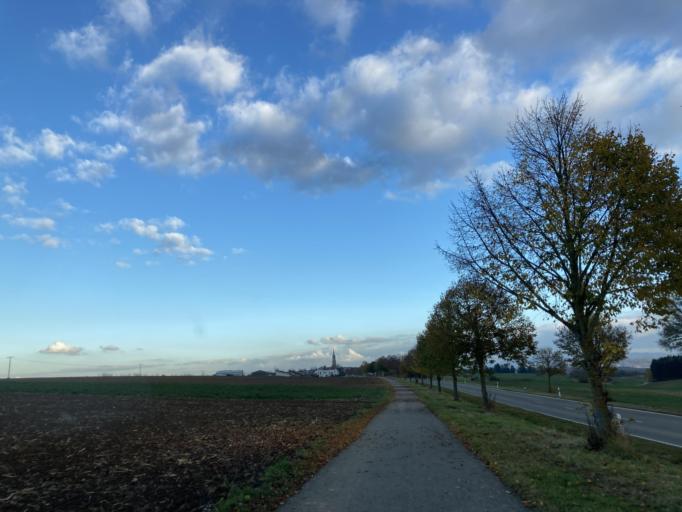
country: DE
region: Baden-Wuerttemberg
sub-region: Tuebingen Region
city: Haigerloch
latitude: 48.4323
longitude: 8.7972
